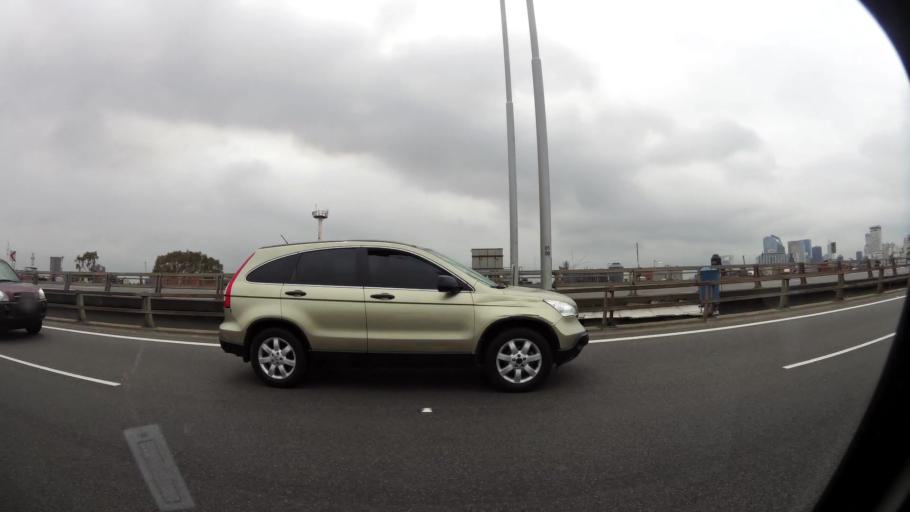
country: AR
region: Buenos Aires F.D.
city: Retiro
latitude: -34.5852
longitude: -58.3801
